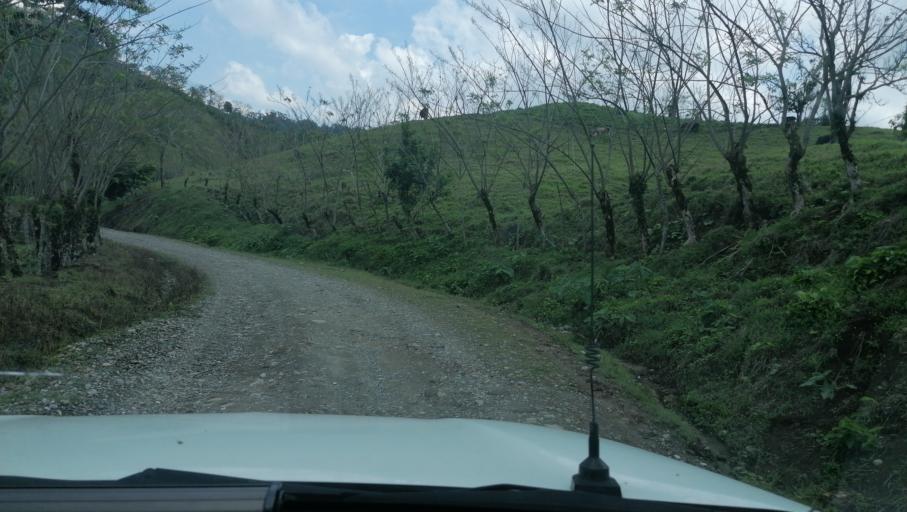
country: MX
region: Chiapas
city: Ixtacomitan
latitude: 17.4411
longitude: -93.2004
